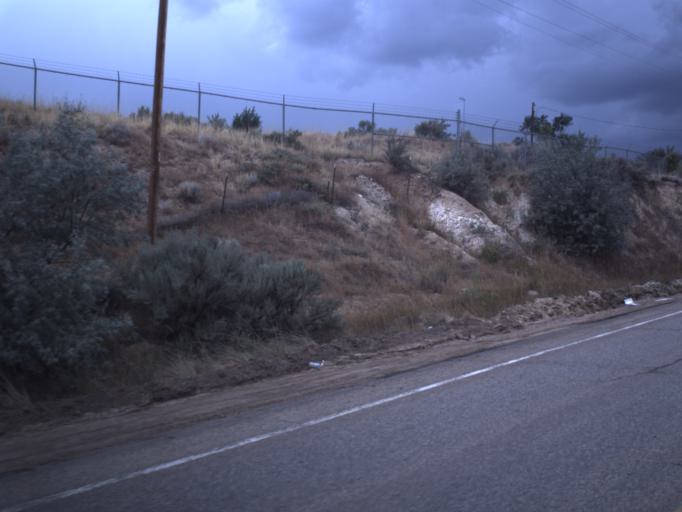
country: US
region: Utah
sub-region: Duchesne County
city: Roosevelt
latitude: 40.3439
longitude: -110.0266
